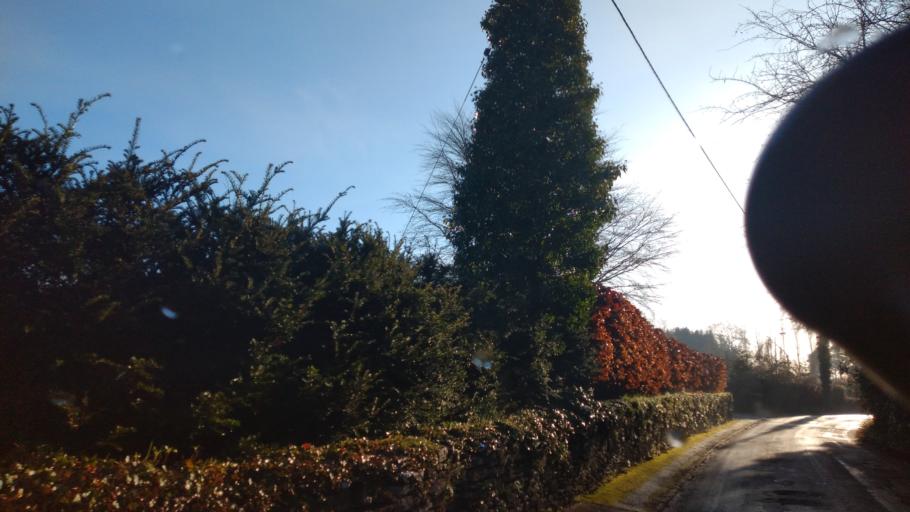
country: GB
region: England
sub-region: Wiltshire
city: Lacock
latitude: 51.4259
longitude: -2.1300
